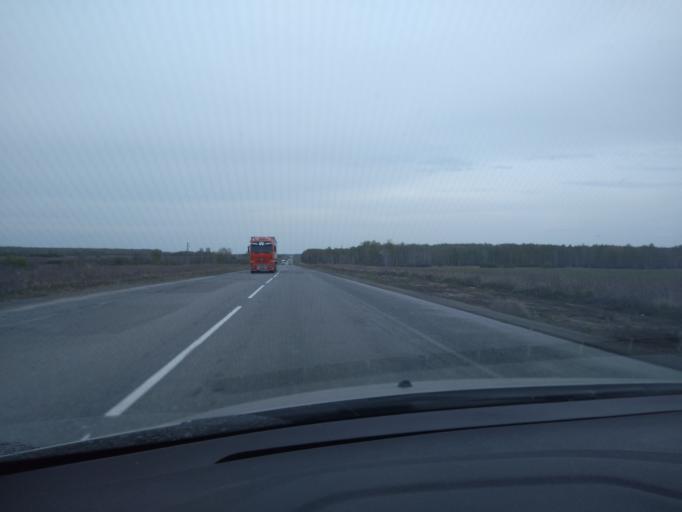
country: RU
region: Sverdlovsk
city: Pyshma
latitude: 56.8892
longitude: 63.0260
